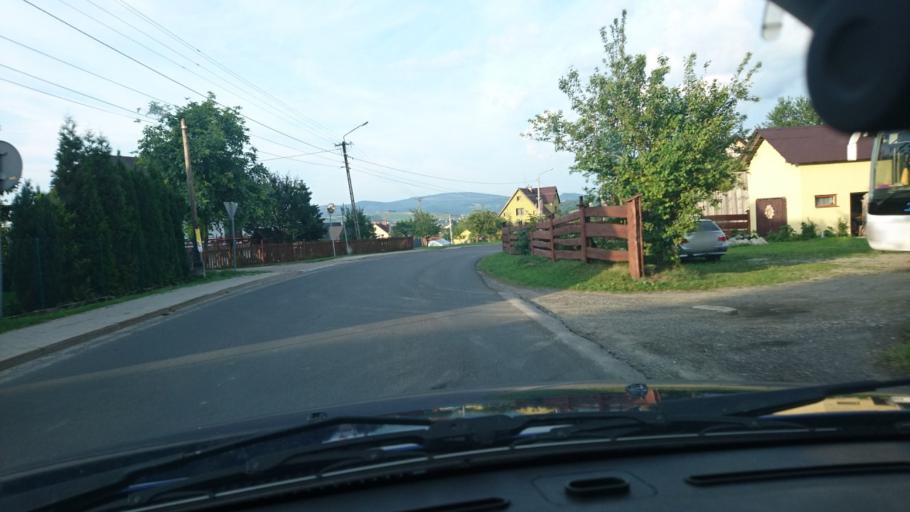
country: PL
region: Silesian Voivodeship
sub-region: Powiat cieszynski
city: Jaworzynka
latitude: 49.5430
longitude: 18.8746
